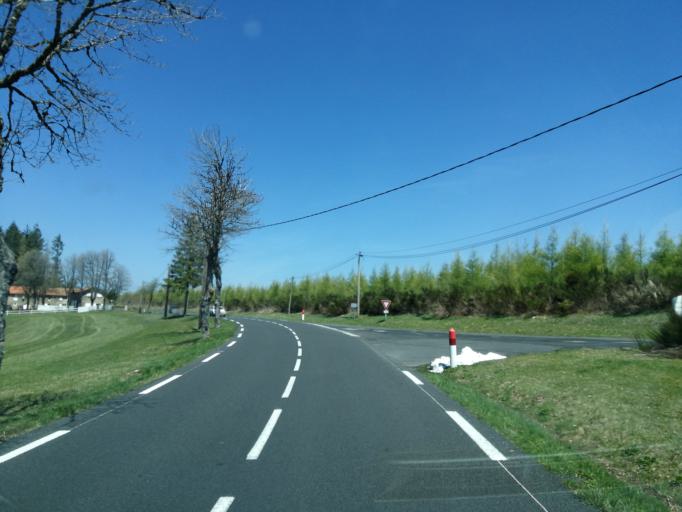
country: FR
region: Rhone-Alpes
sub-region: Departement de l'Ardeche
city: Saint-Agreve
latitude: 45.0769
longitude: 4.3872
